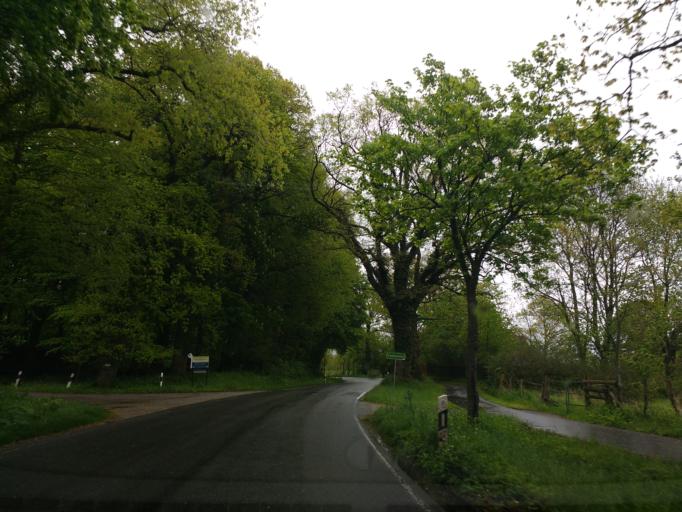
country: DE
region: Schleswig-Holstein
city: Waabs
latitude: 54.5197
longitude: 9.9470
